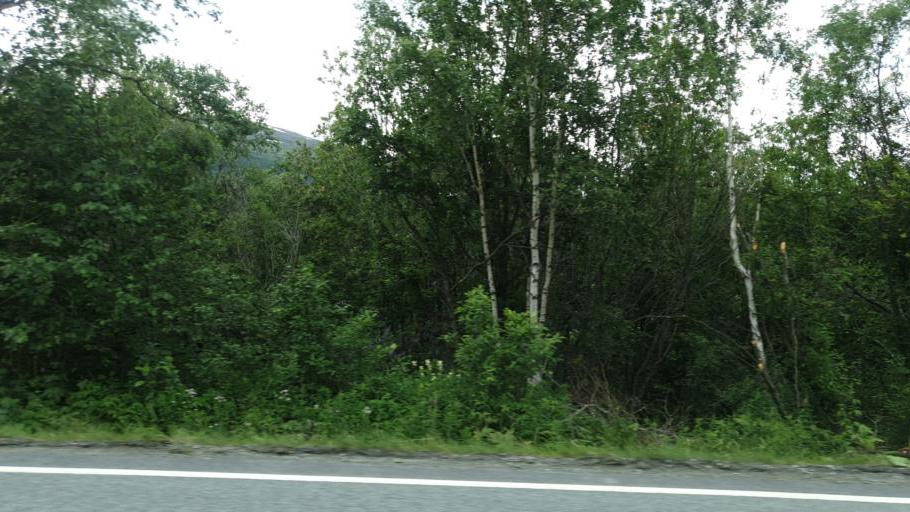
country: NO
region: Sor-Trondelag
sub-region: Oppdal
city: Oppdal
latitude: 62.5545
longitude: 9.6336
